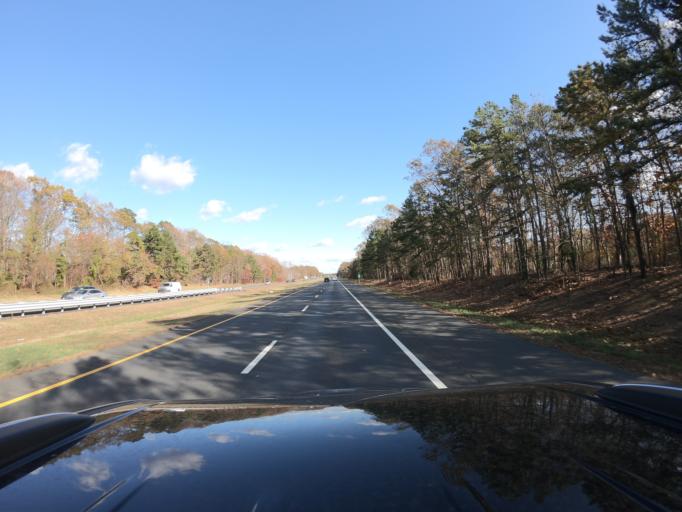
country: US
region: New Jersey
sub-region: Monmouth County
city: Farmingdale
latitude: 40.1669
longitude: -74.2062
